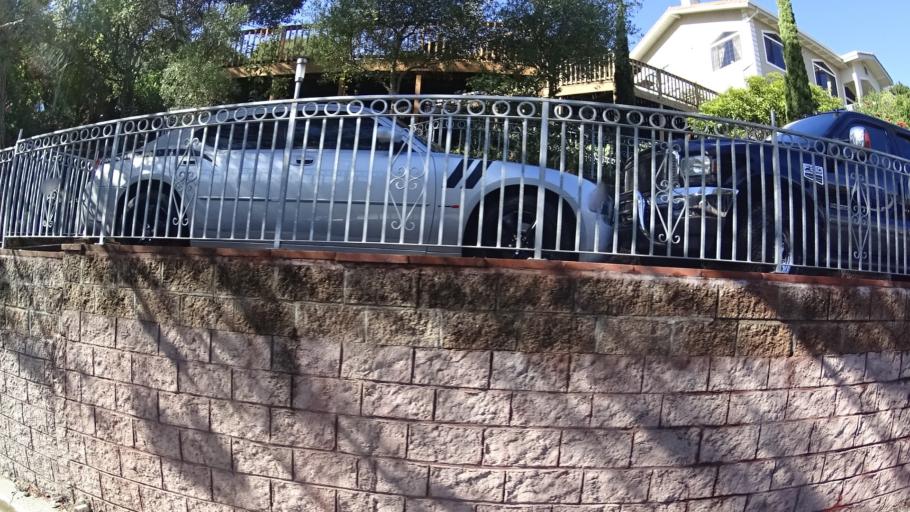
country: US
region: California
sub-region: San Mateo County
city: Millbrae
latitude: 37.5917
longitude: -122.4097
